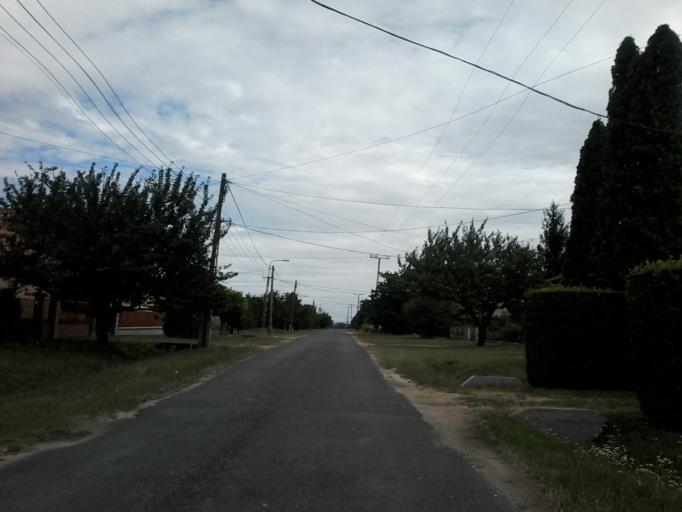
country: HU
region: Vas
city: Janoshaza
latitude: 47.1599
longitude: 17.0406
